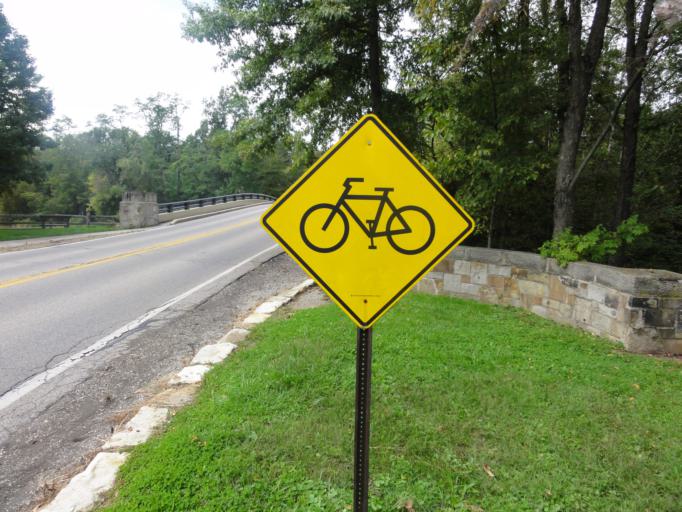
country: US
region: Ohio
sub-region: Cuyahoga County
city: Berea
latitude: 41.3633
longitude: -81.8549
